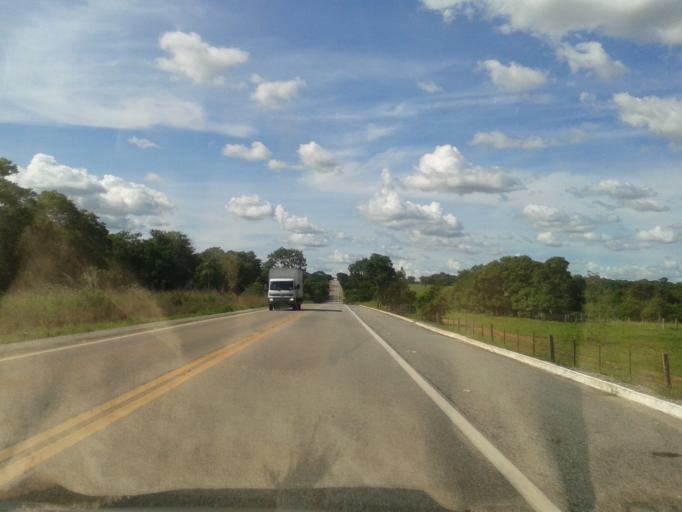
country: BR
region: Goias
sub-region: Mozarlandia
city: Mozarlandia
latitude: -15.1198
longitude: -50.6044
